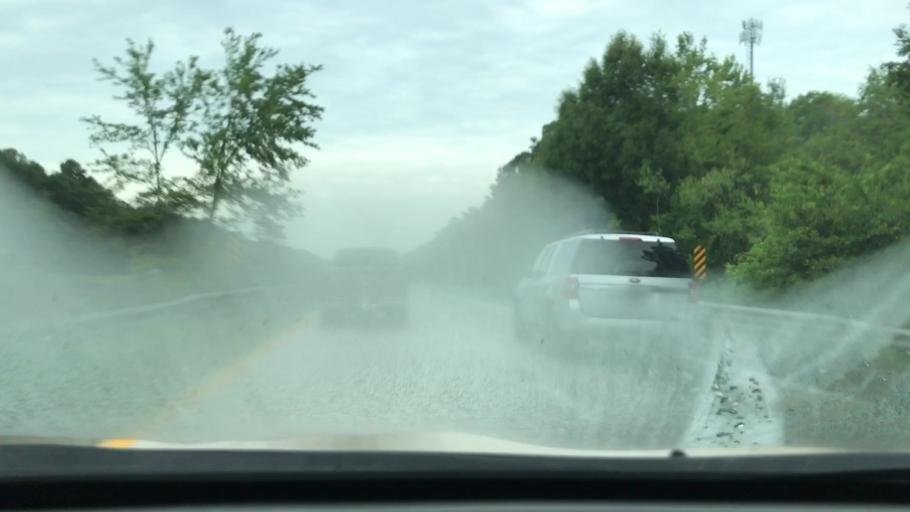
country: US
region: South Carolina
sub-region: Jasper County
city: Hardeeville
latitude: 32.3546
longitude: -81.0415
